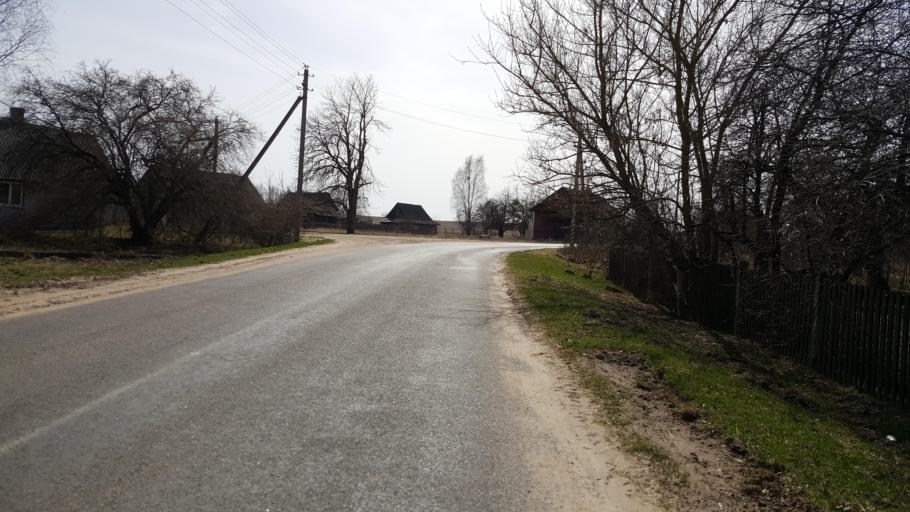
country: BY
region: Brest
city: Kamyanyuki
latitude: 52.4812
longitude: 23.8769
